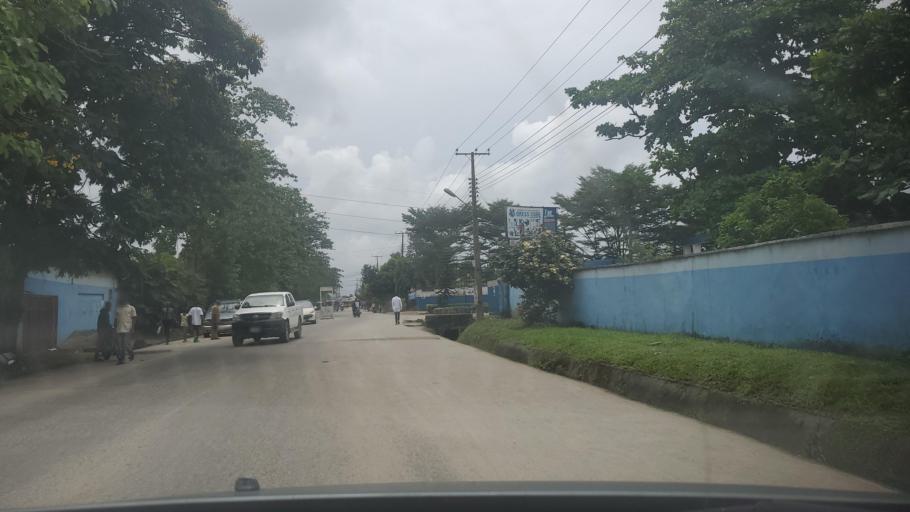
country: NG
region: Rivers
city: Emuoha
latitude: 4.9014
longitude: 6.9063
